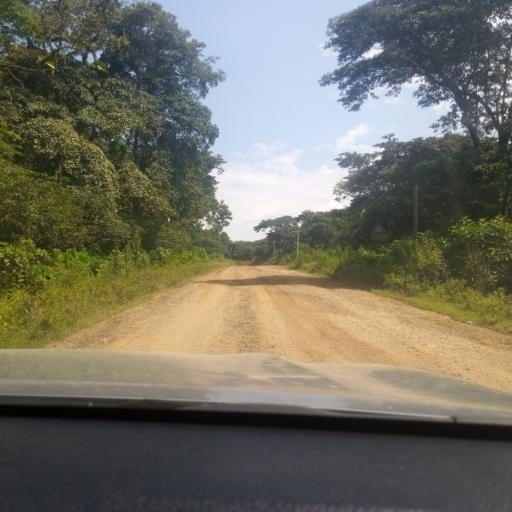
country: ET
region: Southern Nations, Nationalities, and People's Region
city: Tippi
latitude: 7.0720
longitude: 35.4309
